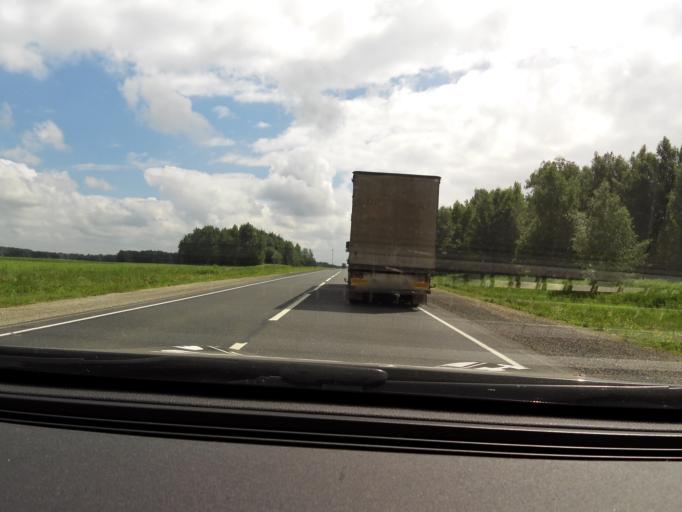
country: RU
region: Perm
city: Orda
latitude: 57.2073
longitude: 57.0991
